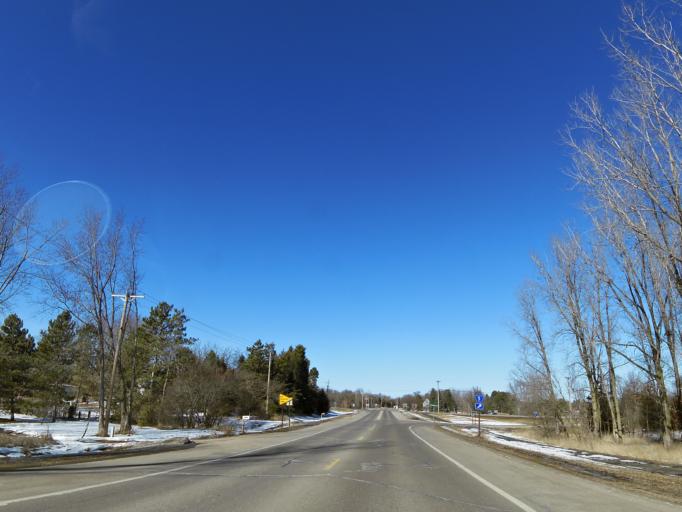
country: US
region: Minnesota
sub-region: Washington County
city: Stillwater
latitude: 45.0761
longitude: -92.8289
